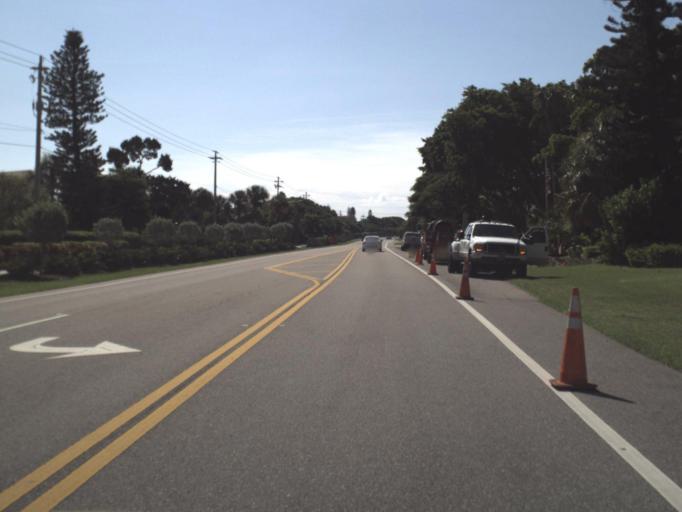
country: US
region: Florida
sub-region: Manatee County
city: Longboat Key
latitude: 27.4026
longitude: -82.6502
